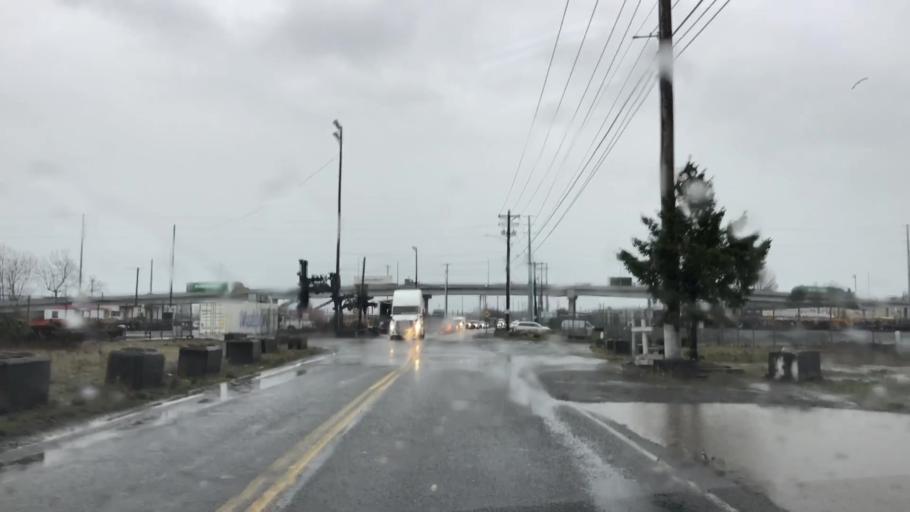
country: US
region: Washington
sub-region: Pierce County
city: Tacoma
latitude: 47.2577
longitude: -122.4075
